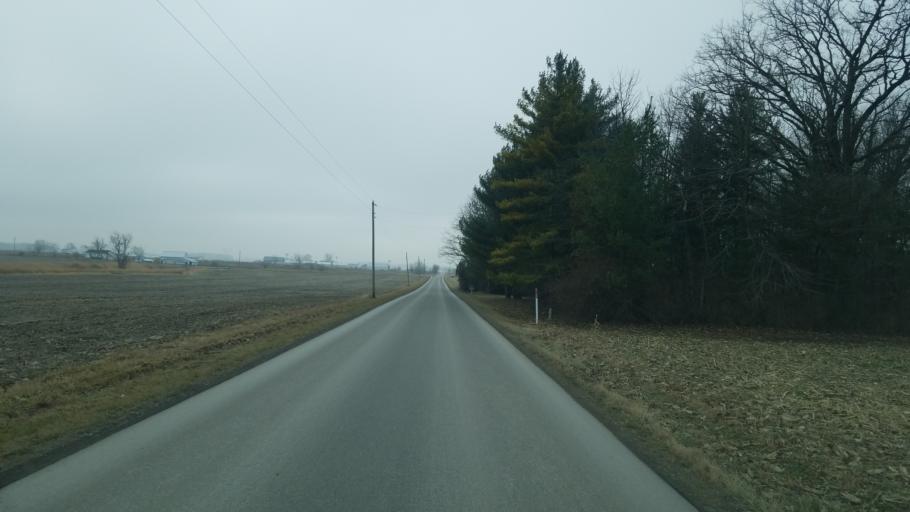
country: US
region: Indiana
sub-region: Adams County
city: Berne
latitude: 40.6841
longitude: -84.8981
